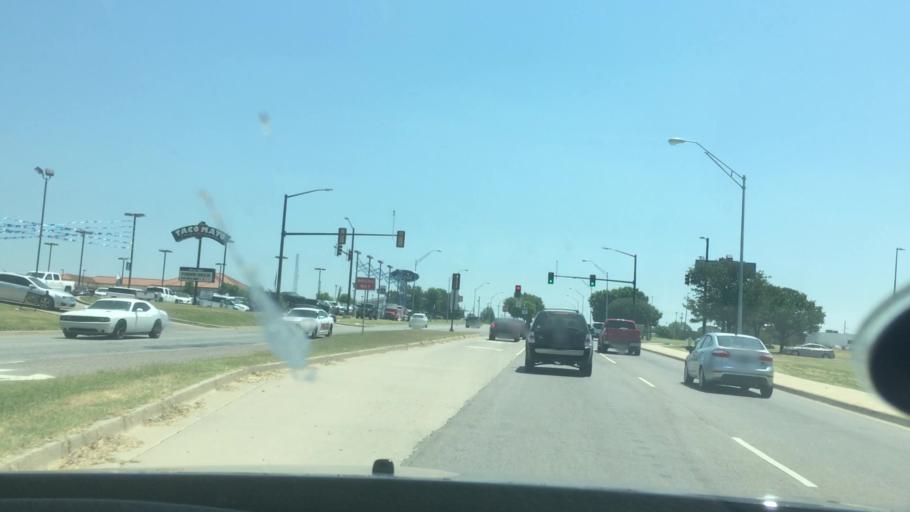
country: US
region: Oklahoma
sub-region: Pontotoc County
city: Ada
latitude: 34.7905
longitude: -96.6564
